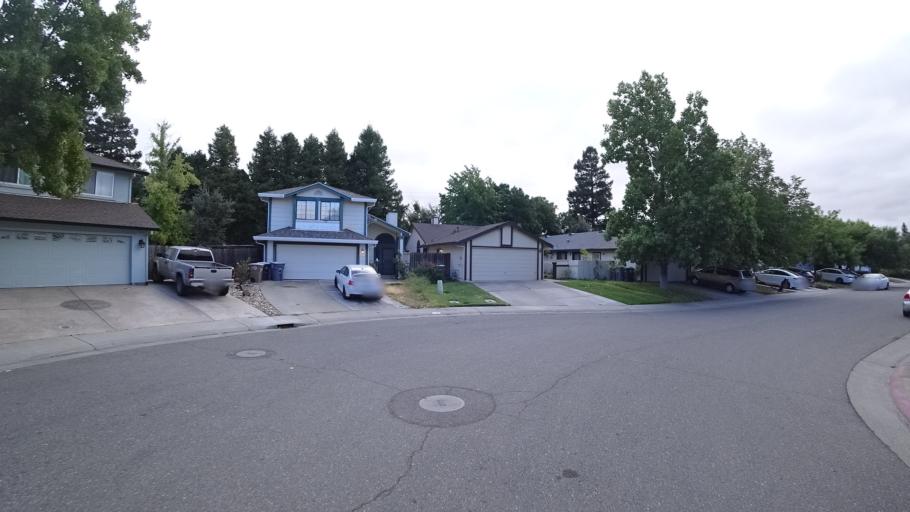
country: US
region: California
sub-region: Sacramento County
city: Laguna
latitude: 38.4183
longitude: -121.4186
